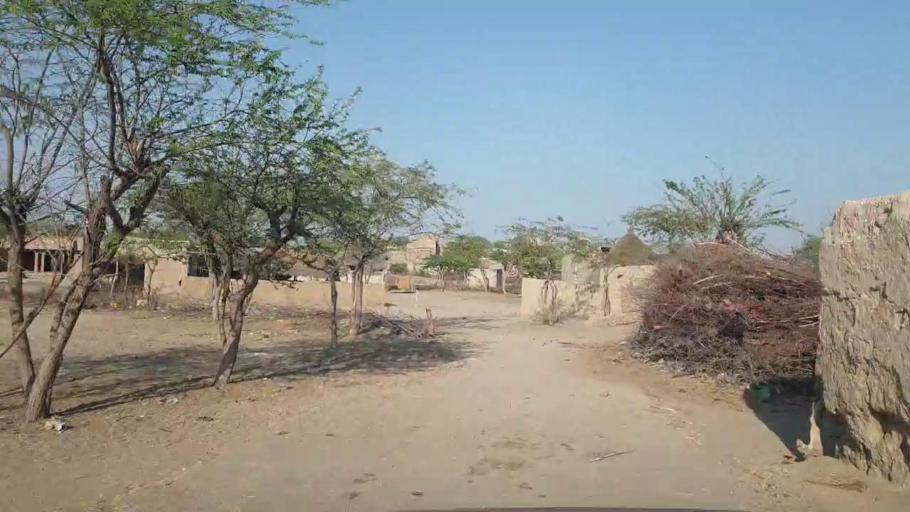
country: PK
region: Sindh
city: Chor
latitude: 25.5443
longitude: 69.7557
